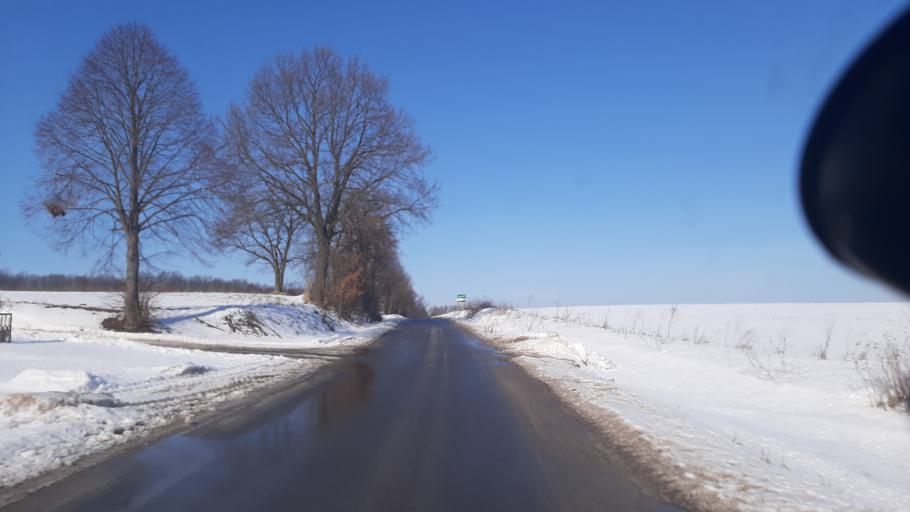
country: PL
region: Lublin Voivodeship
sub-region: Powiat pulawski
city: Naleczow
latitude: 51.2914
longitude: 22.2706
